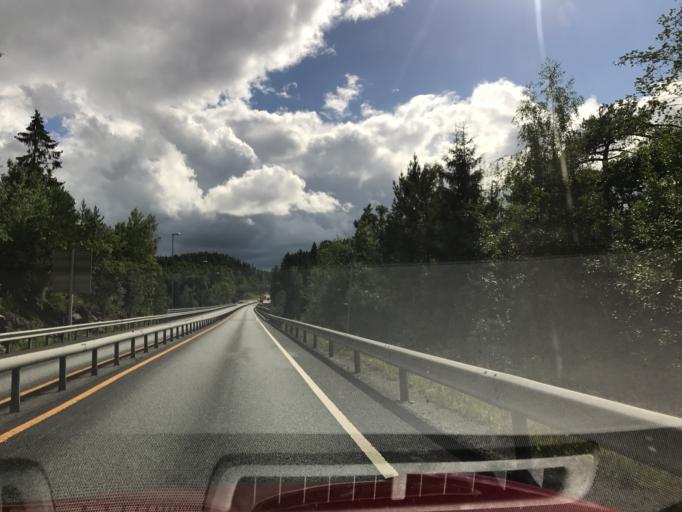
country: NO
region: Aust-Agder
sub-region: Gjerstad
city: Gjerstad
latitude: 58.8363
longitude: 9.0922
